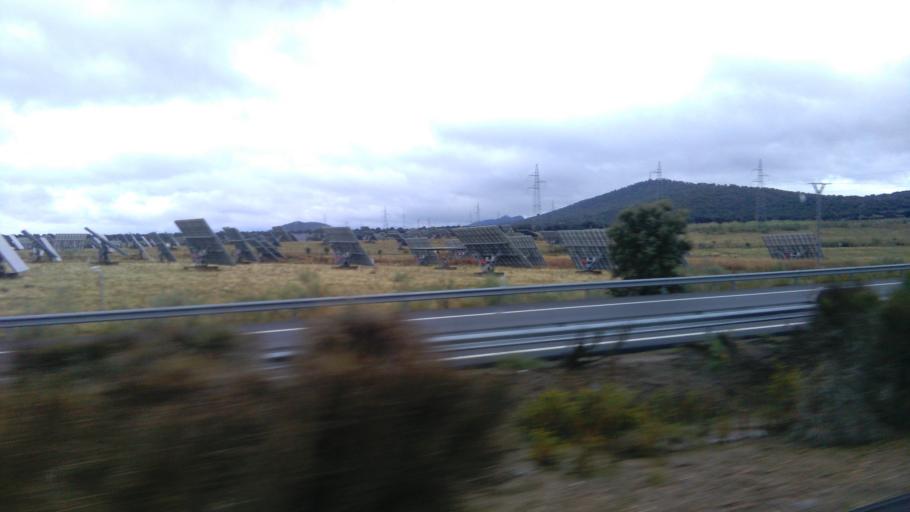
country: ES
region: Extremadura
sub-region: Provincia de Caceres
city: Almaraz
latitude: 39.8221
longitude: -5.6611
